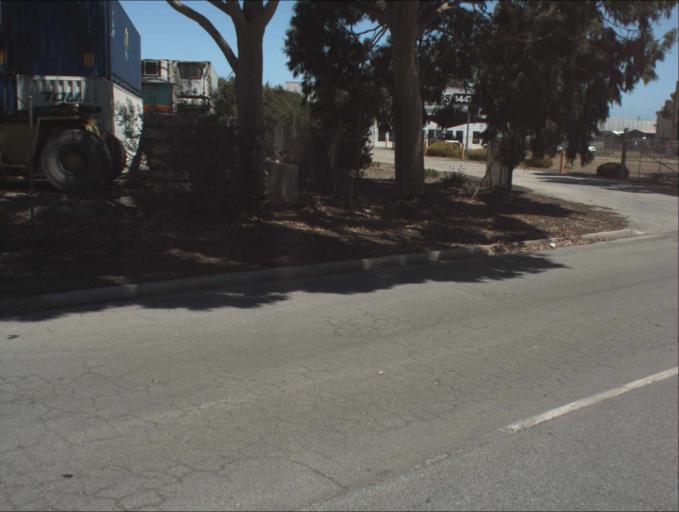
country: AU
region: South Australia
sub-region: Port Adelaide Enfield
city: Alberton
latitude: -34.8385
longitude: 138.5328
